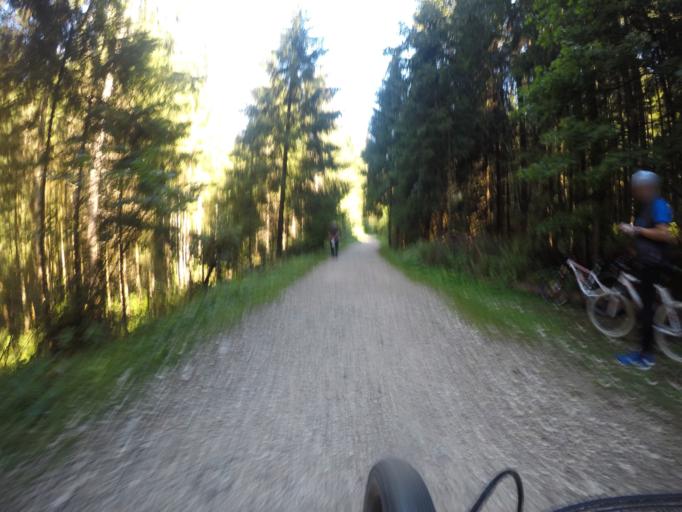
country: IT
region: Veneto
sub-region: Provincia di Vicenza
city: Canove di Roana
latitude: 45.8513
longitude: 11.4772
